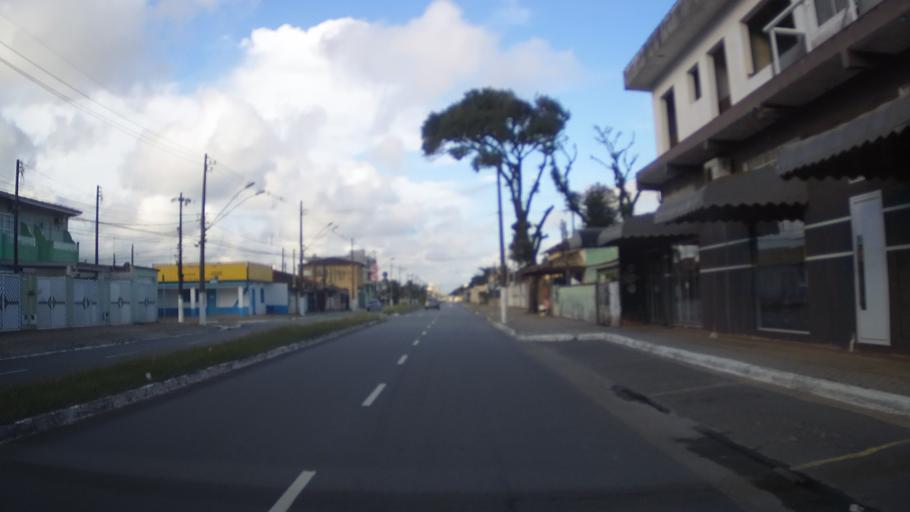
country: BR
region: Sao Paulo
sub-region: Mongagua
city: Mongagua
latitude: -24.0761
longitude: -46.5853
